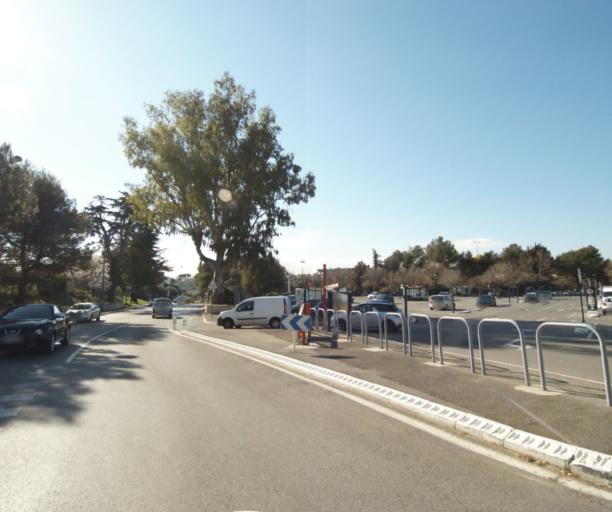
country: FR
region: Provence-Alpes-Cote d'Azur
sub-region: Departement des Alpes-Maritimes
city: Biot
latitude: 43.6033
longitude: 7.0918
